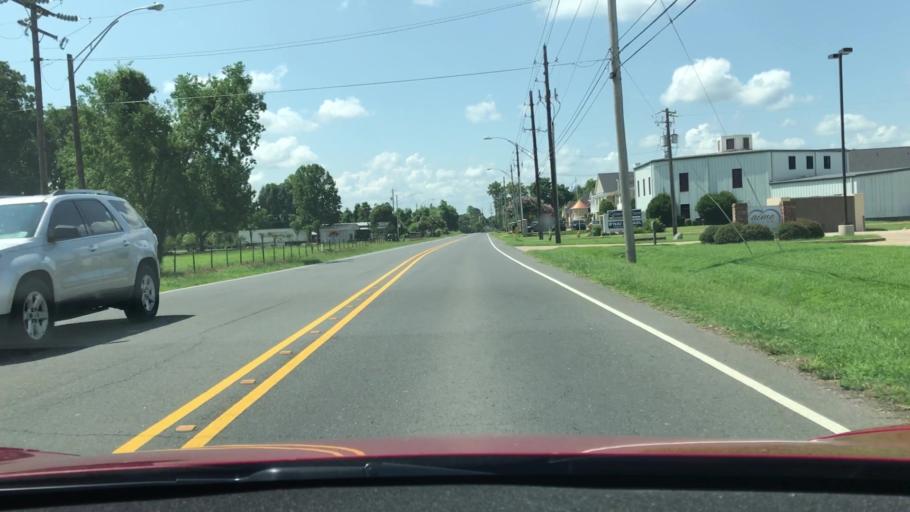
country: US
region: Louisiana
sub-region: Bossier Parish
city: Bossier City
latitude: 32.4221
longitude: -93.6942
